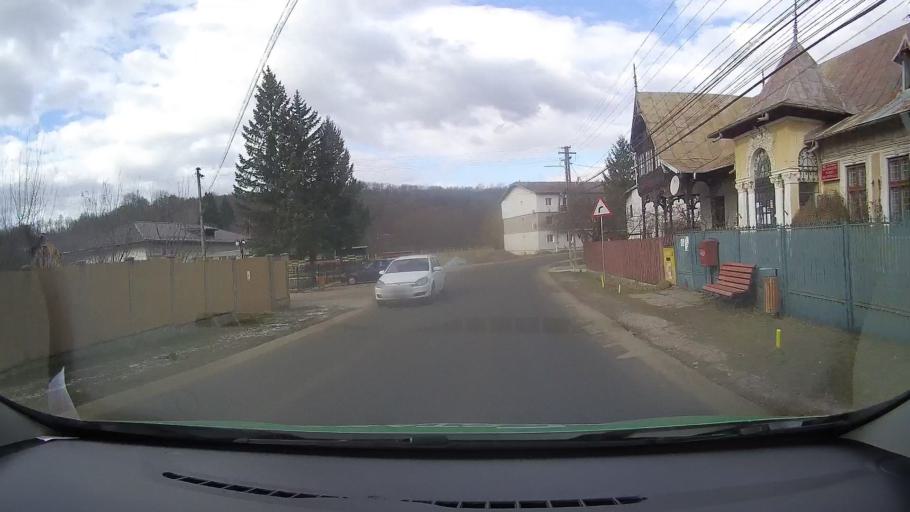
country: RO
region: Prahova
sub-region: Comuna Provita de Sus
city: Provita de Sus
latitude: 45.1356
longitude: 25.6371
